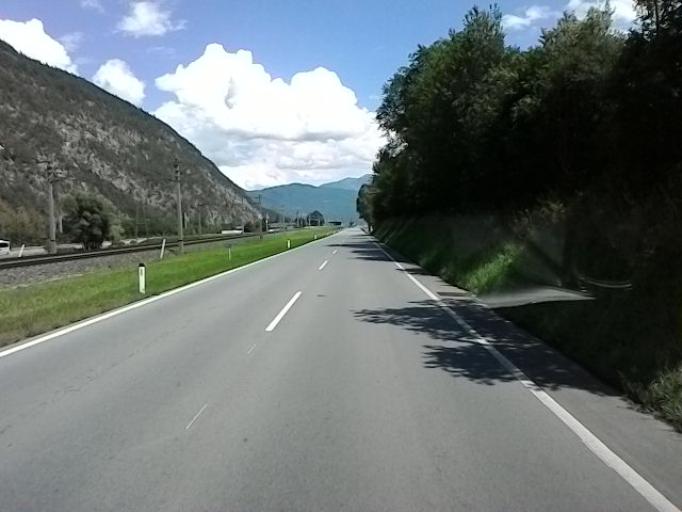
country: AT
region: Tyrol
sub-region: Politischer Bezirk Innsbruck Land
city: Wildermieming
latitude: 47.2907
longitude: 11.0179
